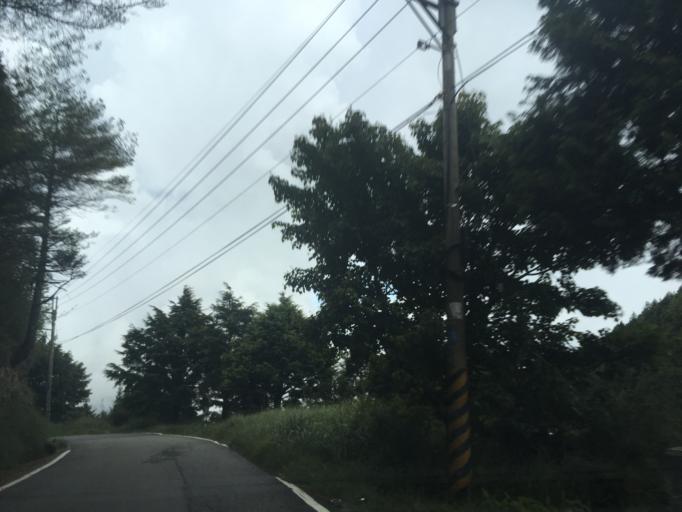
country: TW
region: Taiwan
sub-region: Nantou
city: Puli
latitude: 24.2698
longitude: 121.0313
